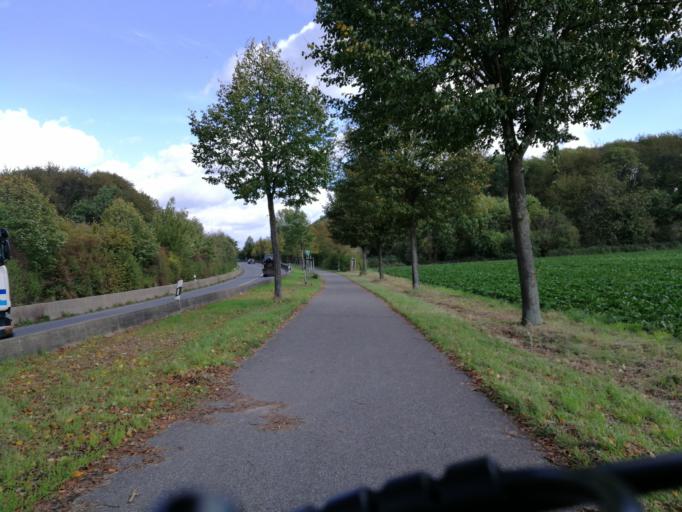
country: DE
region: North Rhine-Westphalia
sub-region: Regierungsbezirk Dusseldorf
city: Neuss
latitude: 51.1412
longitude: 6.7368
